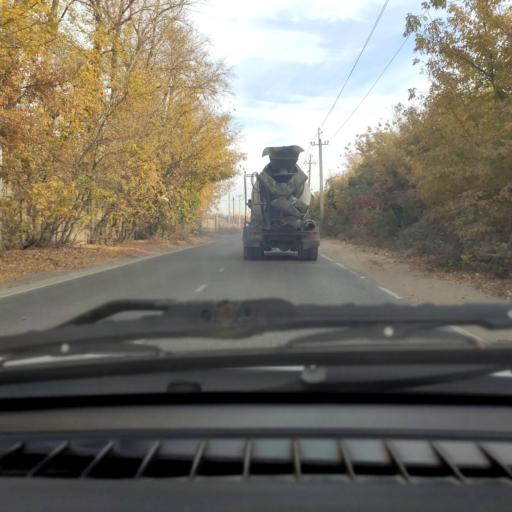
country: RU
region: Samara
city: Zhigulevsk
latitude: 53.5230
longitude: 49.4872
